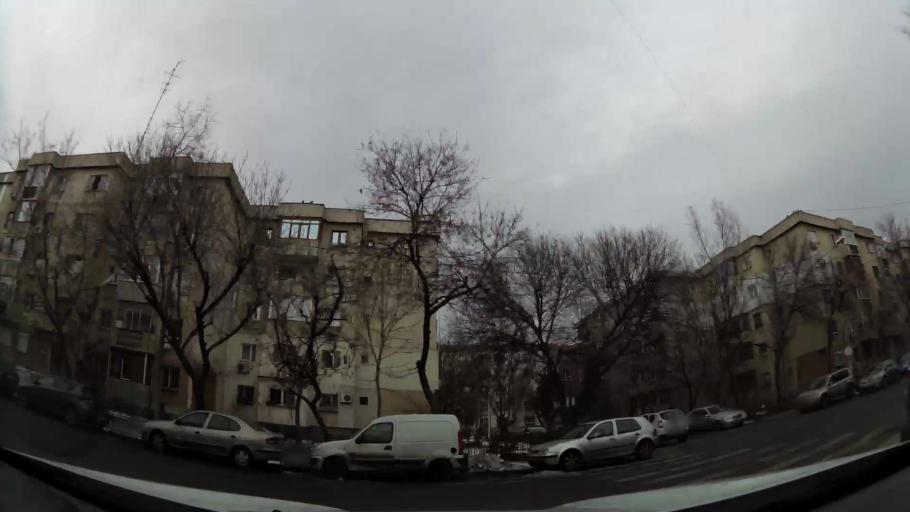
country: RO
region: Bucuresti
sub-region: Municipiul Bucuresti
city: Bucuresti
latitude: 44.4228
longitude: 26.0615
